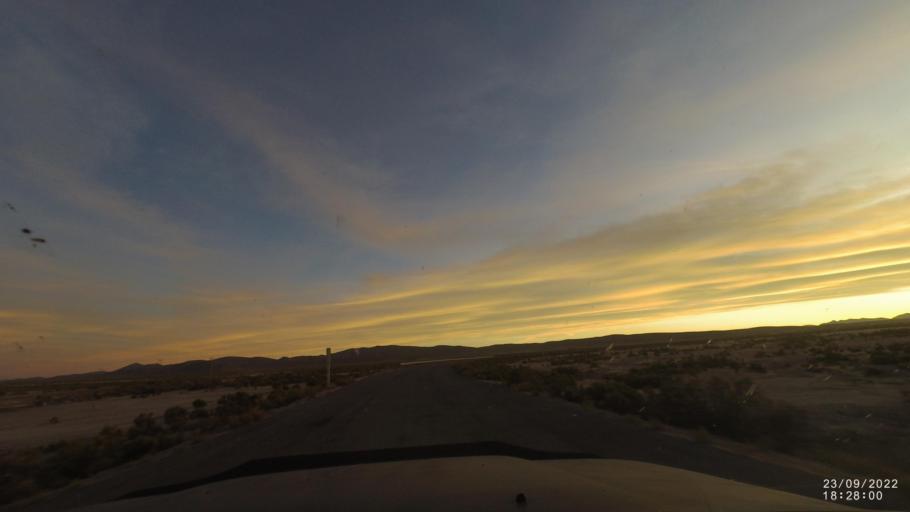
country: BO
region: Oruro
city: Challapata
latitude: -19.3334
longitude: -67.1727
